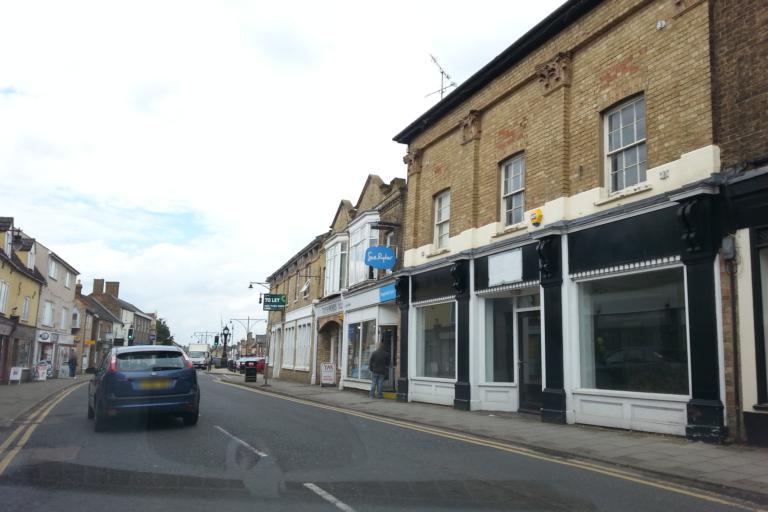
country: GB
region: England
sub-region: Cambridgeshire
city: Ramsey
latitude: 52.4484
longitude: -0.1065
